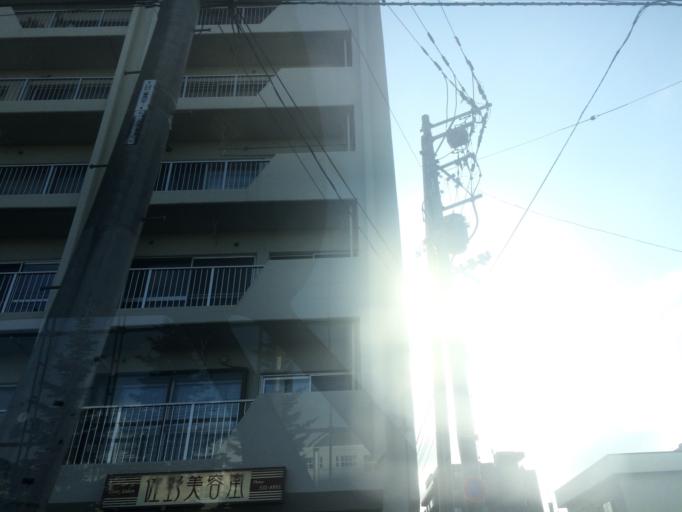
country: JP
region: Hokkaido
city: Sapporo
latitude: 43.0365
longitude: 141.3513
